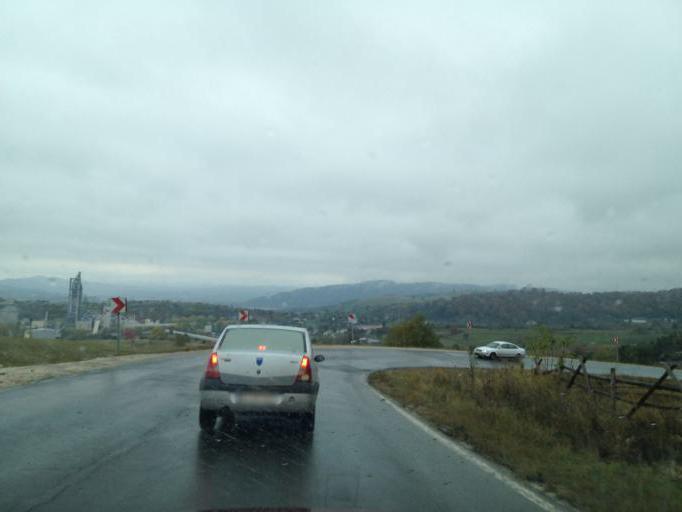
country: RO
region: Arges
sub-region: Comuna Valea Mare-Pravat
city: Valea Mare Pravat
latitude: 45.2949
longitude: 25.1301
